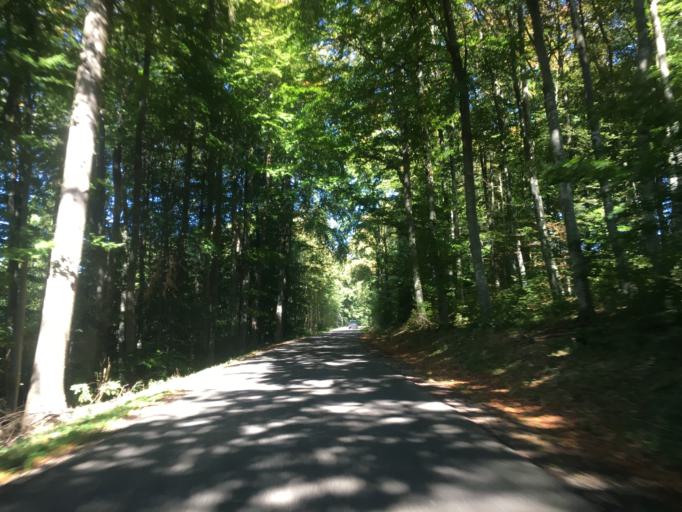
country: DE
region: Baden-Wuerttemberg
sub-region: Tuebingen Region
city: Pfullingen
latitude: 48.4130
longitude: 9.2158
